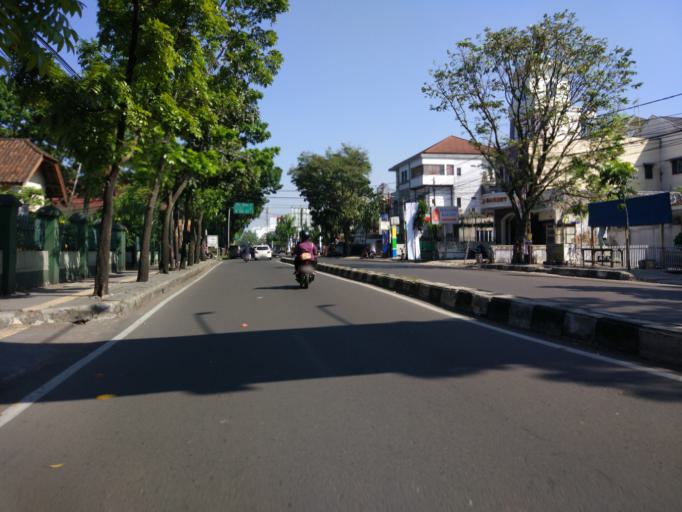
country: ID
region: West Java
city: Bandung
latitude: -6.9253
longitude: 107.6305
